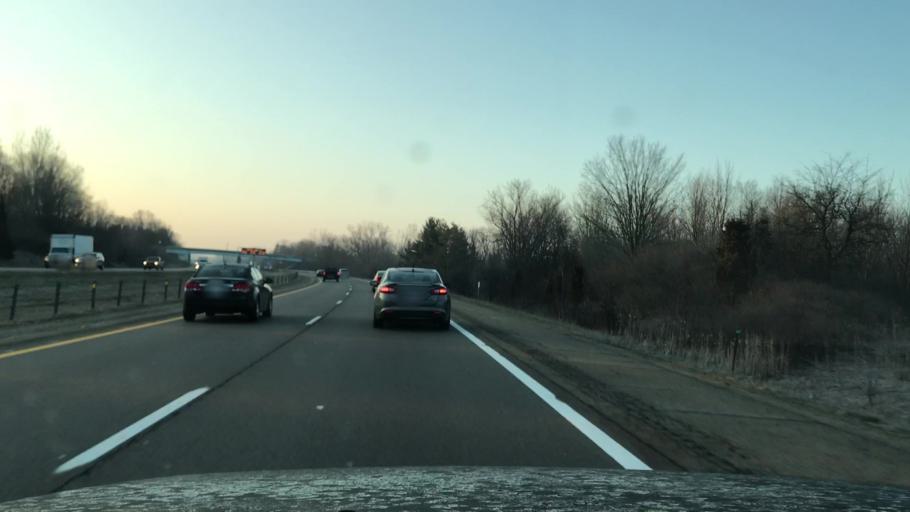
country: US
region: Michigan
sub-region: Kent County
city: East Grand Rapids
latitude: 42.9317
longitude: -85.5634
